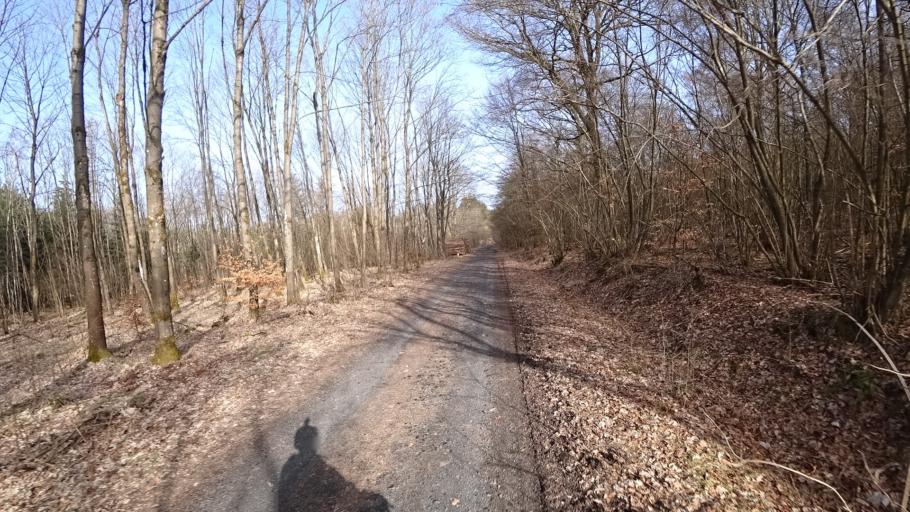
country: DE
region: Rheinland-Pfalz
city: Dickendorf
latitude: 50.7212
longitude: 7.8506
